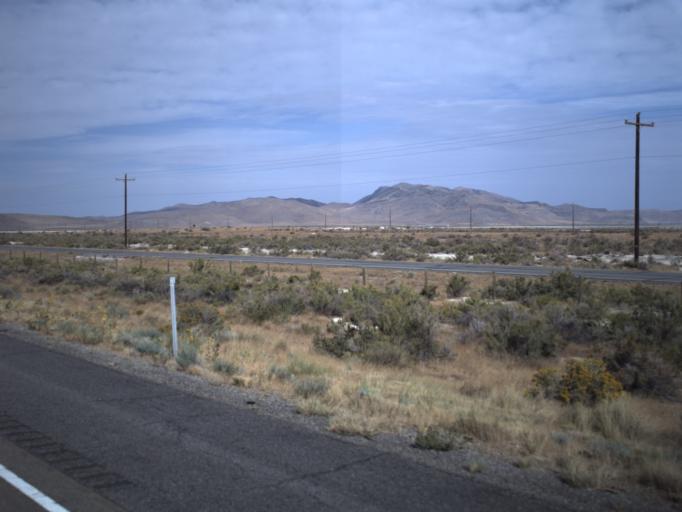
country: US
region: Utah
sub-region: Tooele County
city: Grantsville
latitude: 40.7495
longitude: -112.6863
